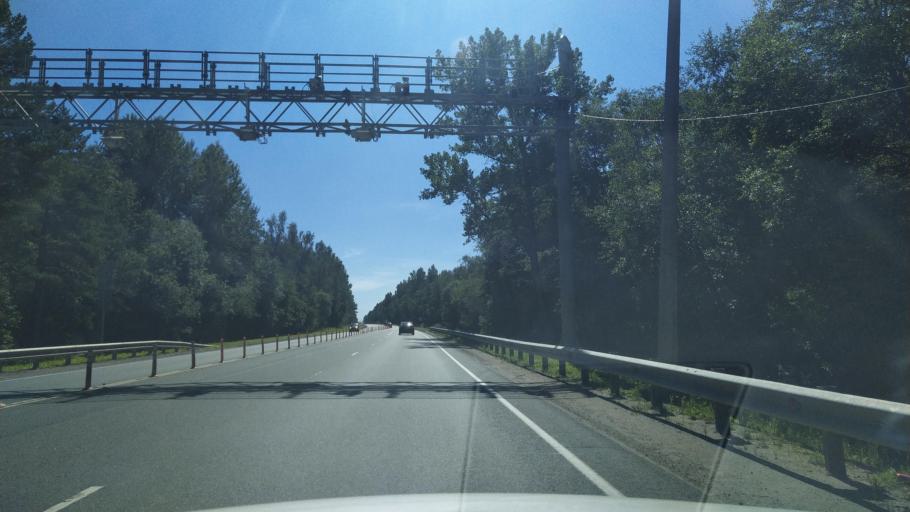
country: RU
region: Pskov
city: Pskov
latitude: 57.7317
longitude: 28.3583
